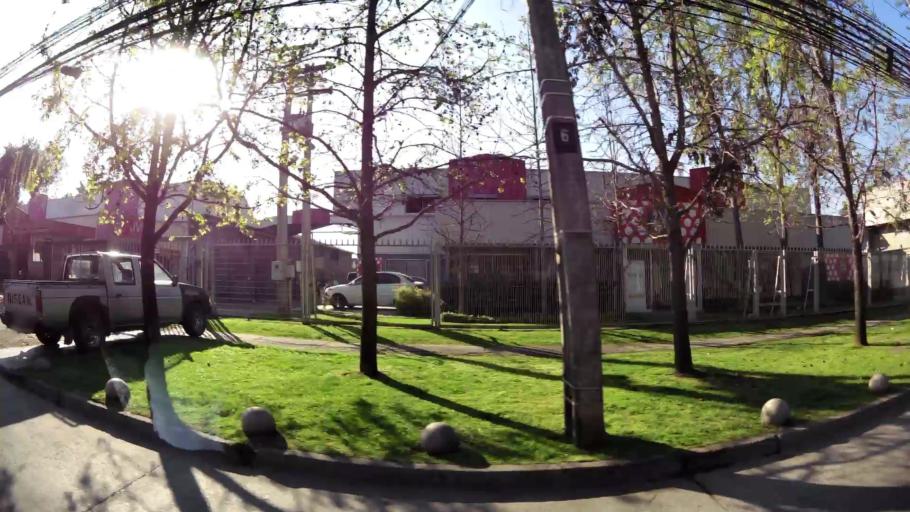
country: CL
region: Santiago Metropolitan
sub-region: Provincia de Santiago
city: Santiago
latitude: -33.3756
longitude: -70.6513
